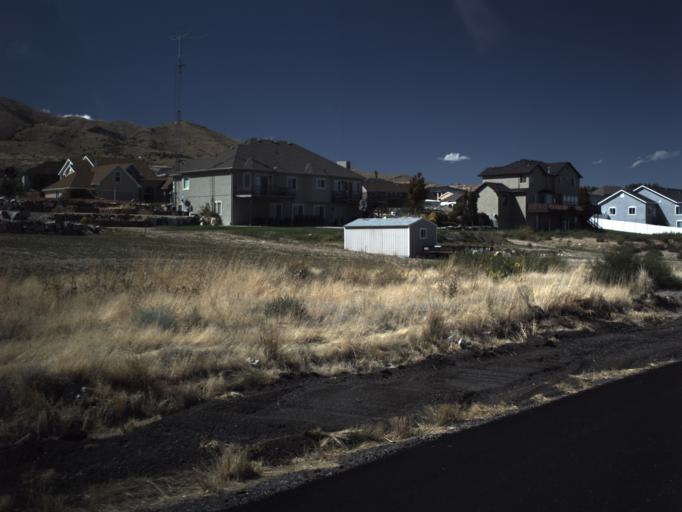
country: US
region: Utah
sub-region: Utah County
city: Saratoga Springs
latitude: 40.2909
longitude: -111.8788
